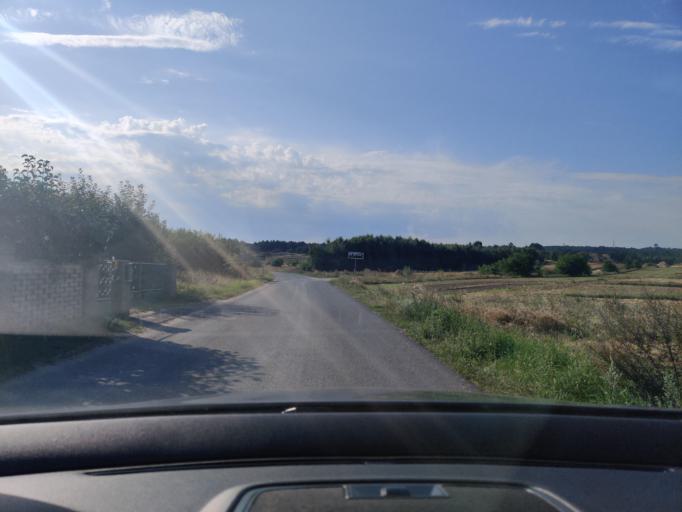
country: PL
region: Greater Poland Voivodeship
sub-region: Konin
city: Konin
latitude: 52.1878
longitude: 18.3233
